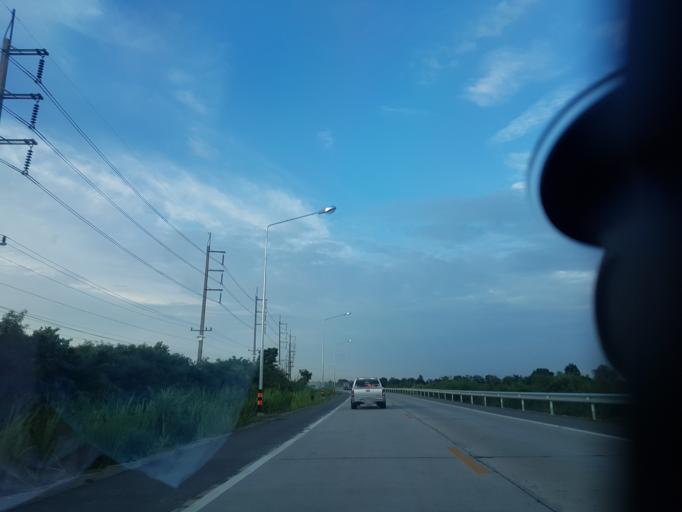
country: TH
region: Phra Nakhon Si Ayutthaya
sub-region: Amphoe Tha Ruea
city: Tha Ruea
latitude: 14.5410
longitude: 100.7567
